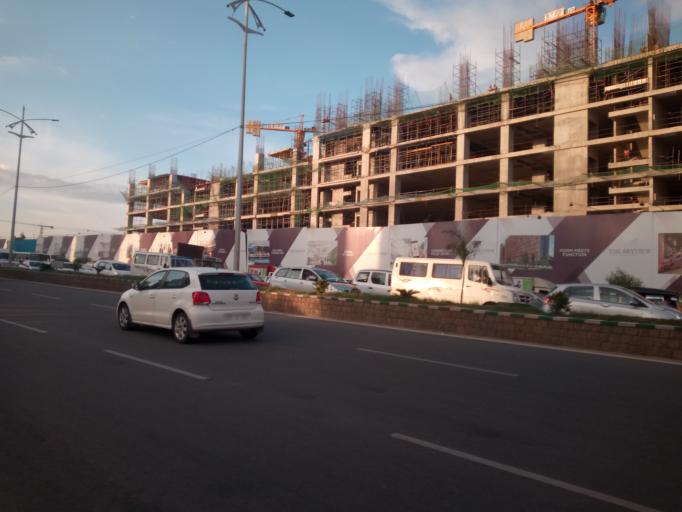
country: IN
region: Telangana
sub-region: Rangareddi
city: Kukatpalli
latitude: 17.4320
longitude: 78.3748
